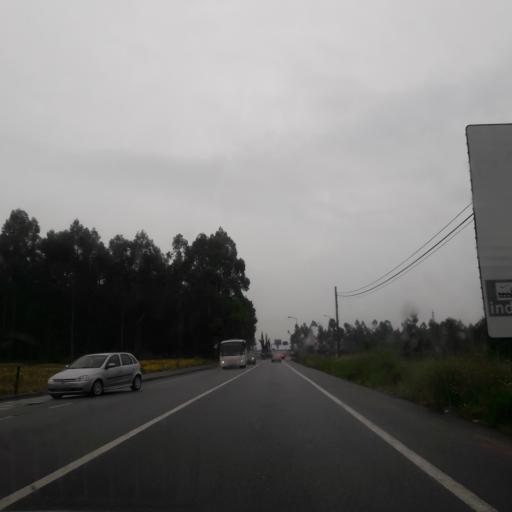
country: PT
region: Porto
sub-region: Vila do Conde
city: Arvore
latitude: 41.3064
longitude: -8.7033
